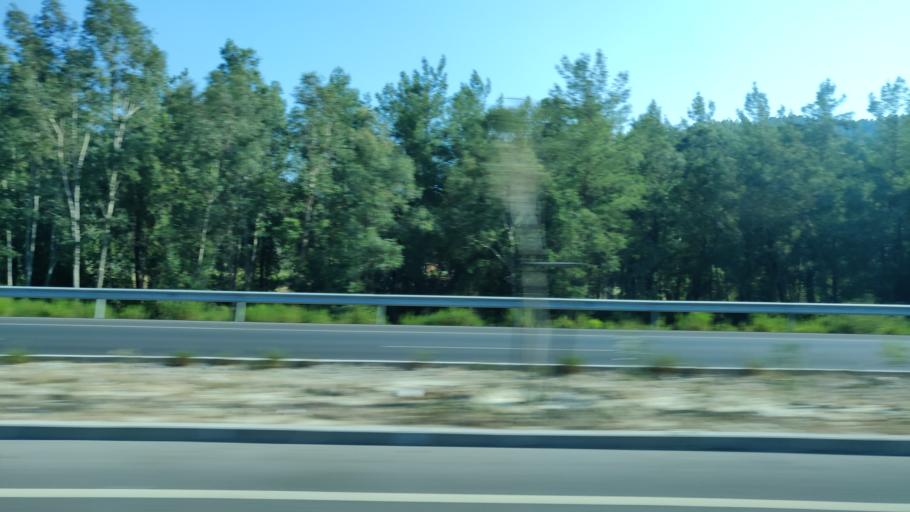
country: TR
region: Mugla
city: Goecek
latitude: 36.7606
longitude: 28.8780
